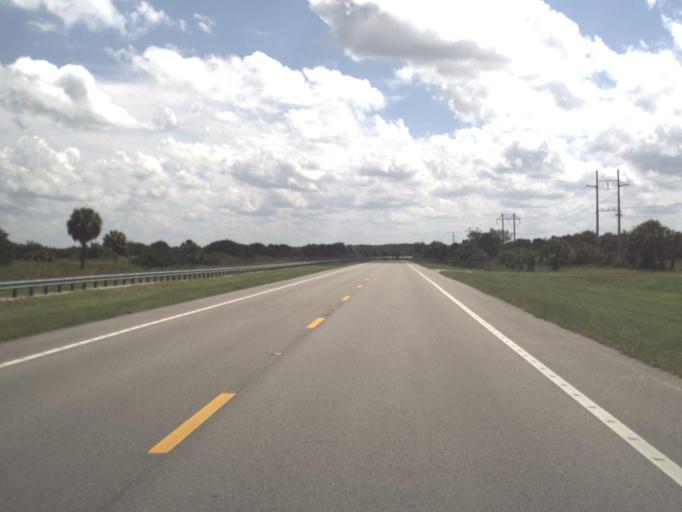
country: US
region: Florida
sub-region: Collier County
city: Immokalee
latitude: 26.3678
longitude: -81.3523
